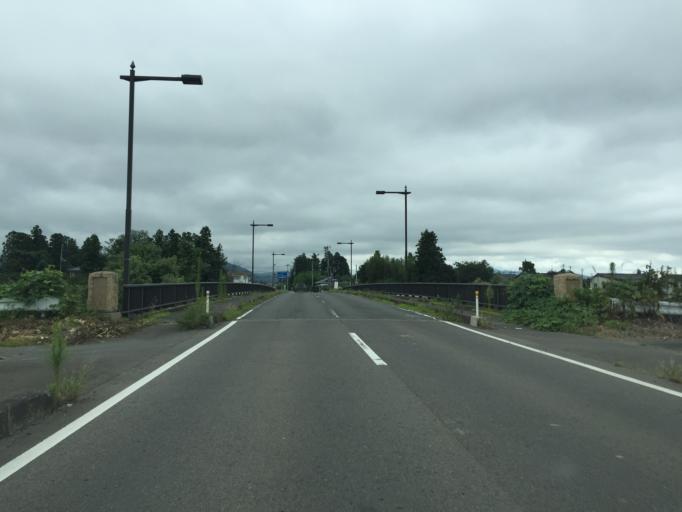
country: JP
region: Fukushima
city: Fukushima-shi
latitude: 37.7550
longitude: 140.4015
